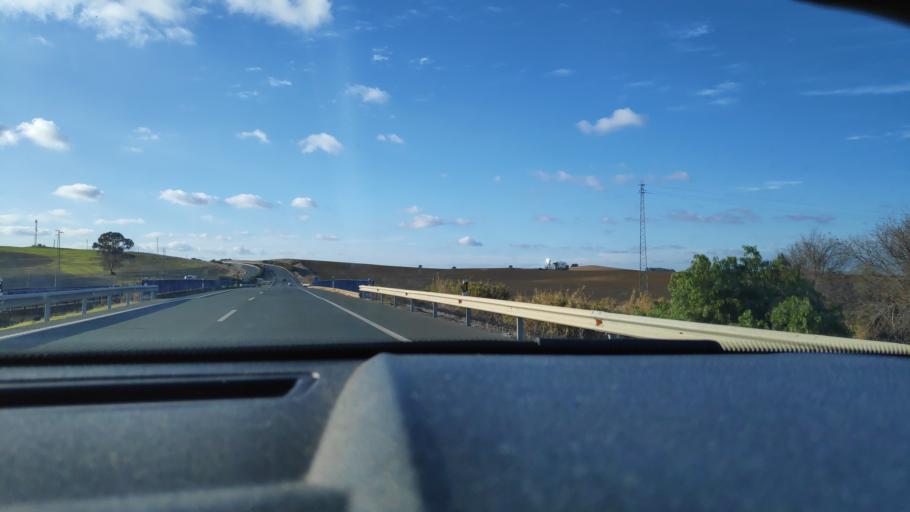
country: ES
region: Andalusia
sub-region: Provincia de Sevilla
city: La Luisiana
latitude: 37.5269
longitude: -5.2878
